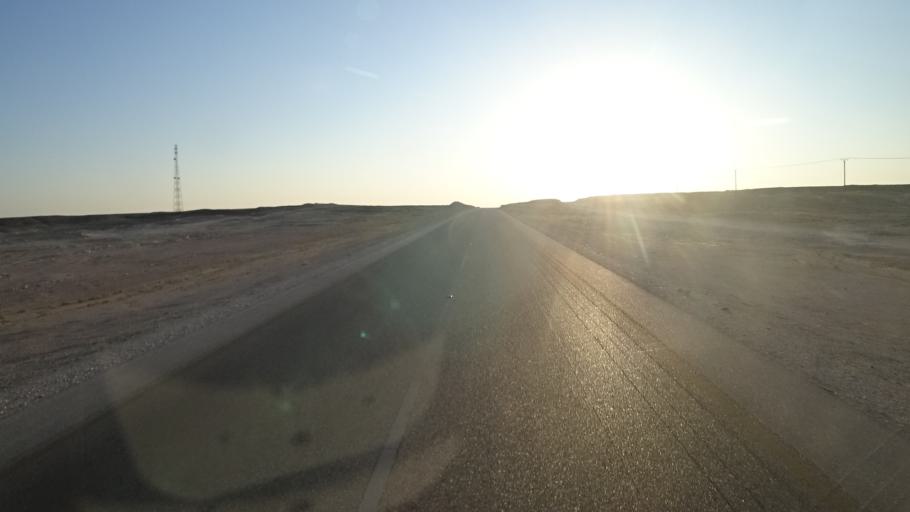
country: OM
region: Zufar
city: Salalah
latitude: 17.5403
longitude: 53.4156
